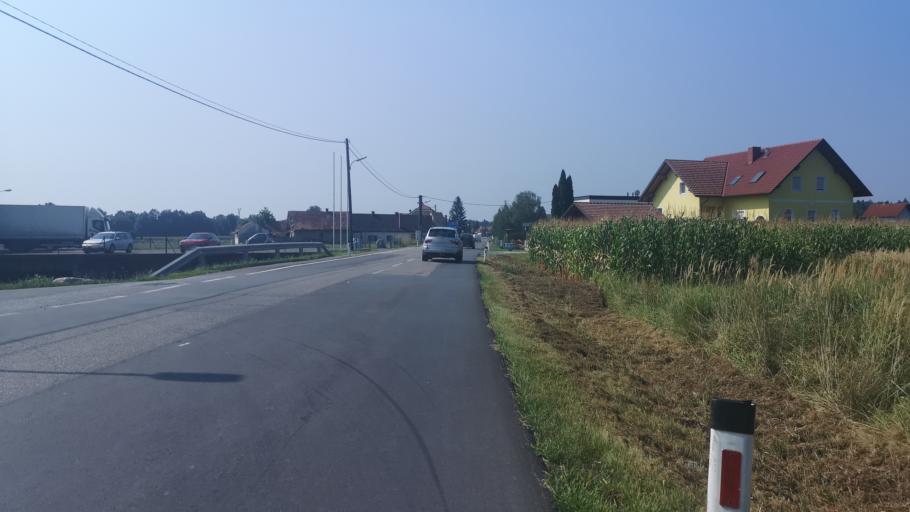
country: AT
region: Styria
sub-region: Politischer Bezirk Graz-Umgebung
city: Seiersberg
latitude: 46.9963
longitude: 15.4003
